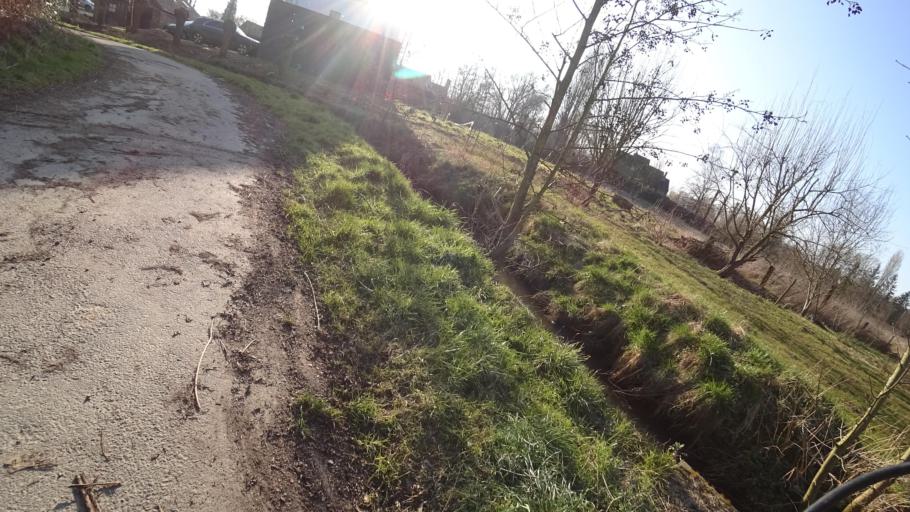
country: BE
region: Wallonia
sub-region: Province du Brabant Wallon
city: Chastre
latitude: 50.5890
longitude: 4.6469
